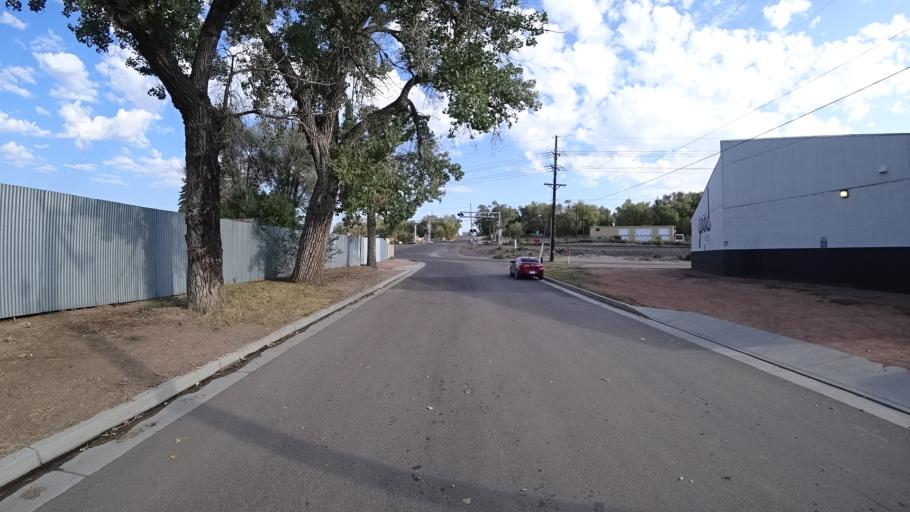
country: US
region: Colorado
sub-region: El Paso County
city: Colorado Springs
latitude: 38.8169
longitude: -104.8154
